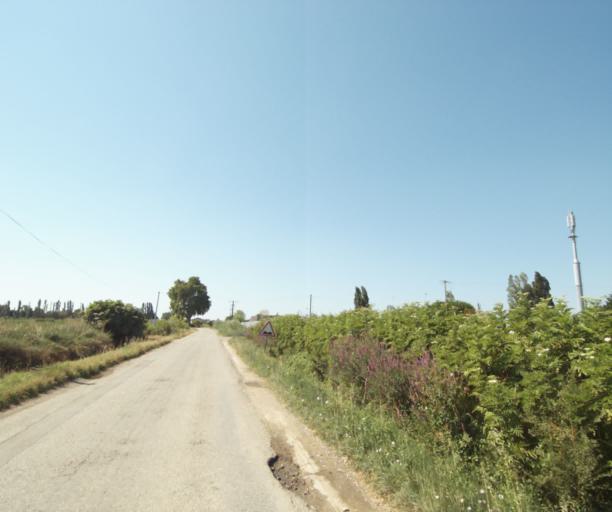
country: FR
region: Languedoc-Roussillon
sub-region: Departement de l'Herault
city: Marsillargues
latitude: 43.6575
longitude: 4.1651
